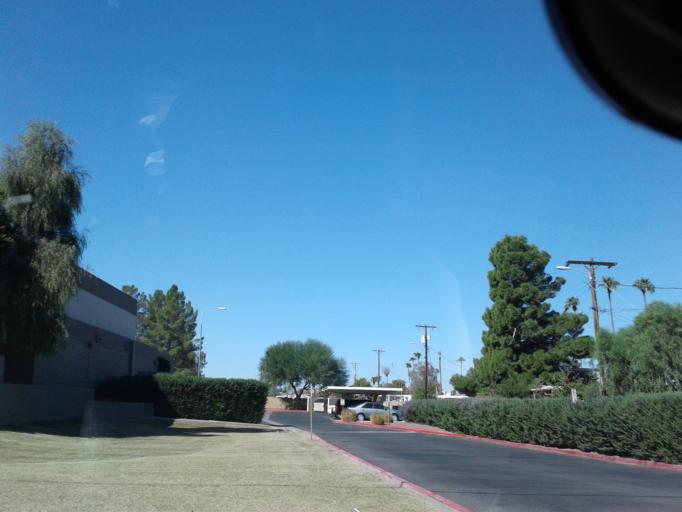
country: US
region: Arizona
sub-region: Maricopa County
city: Tempe
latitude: 33.4605
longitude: -111.9091
